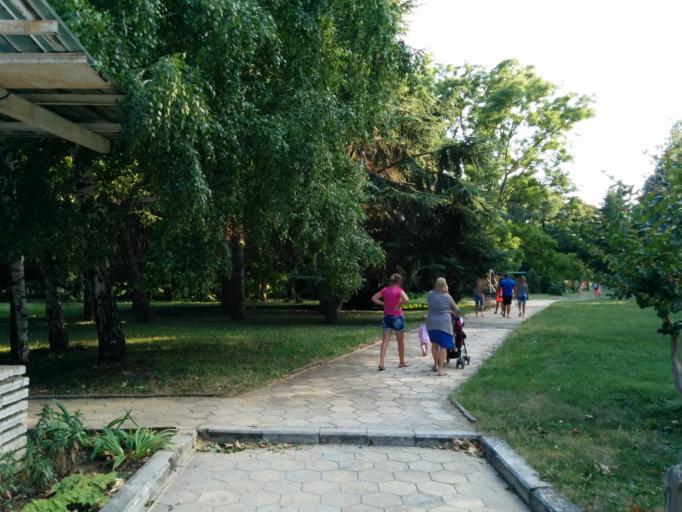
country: BG
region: Varna
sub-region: Obshtina Varna
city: Zlatni Pyasatsi
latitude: 43.2248
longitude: 28.0059
